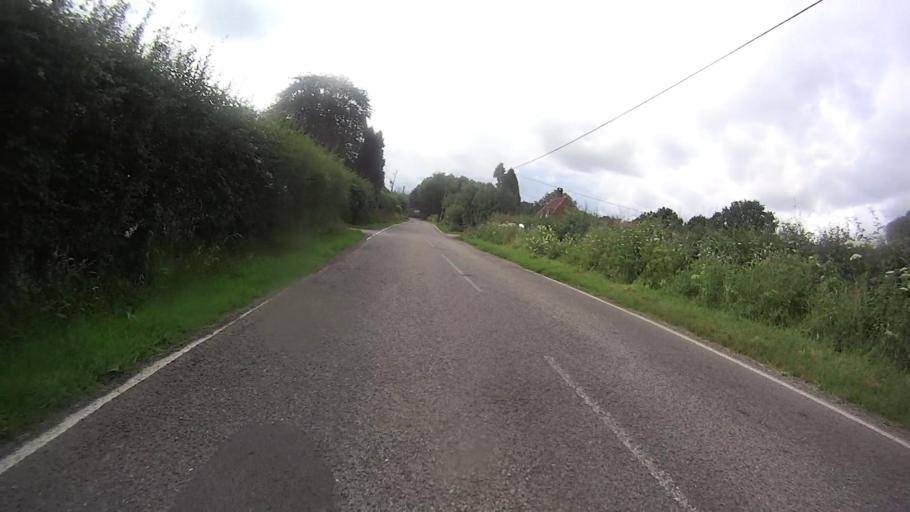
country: GB
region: England
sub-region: Surrey
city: Newdigate
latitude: 51.1696
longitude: -0.2946
